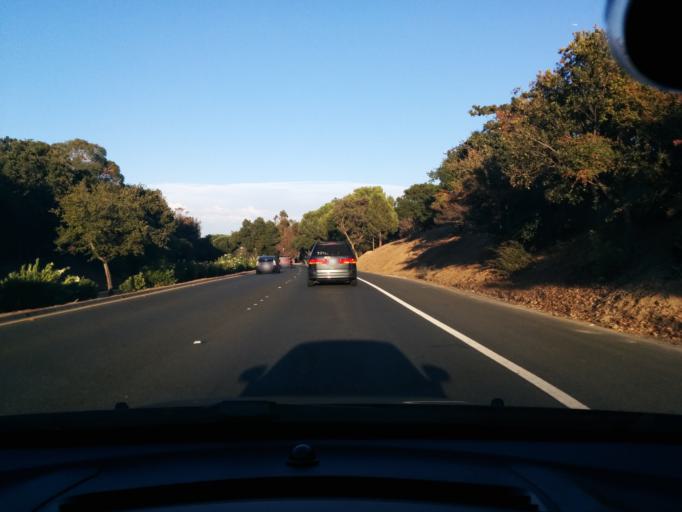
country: US
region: California
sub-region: San Mateo County
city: West Menlo Park
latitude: 37.4215
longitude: -122.2015
